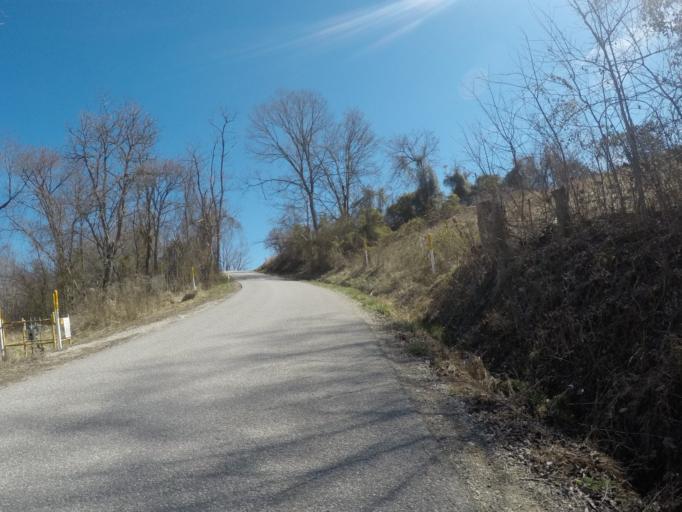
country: US
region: Ohio
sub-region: Lawrence County
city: South Point
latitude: 38.4821
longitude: -82.5685
